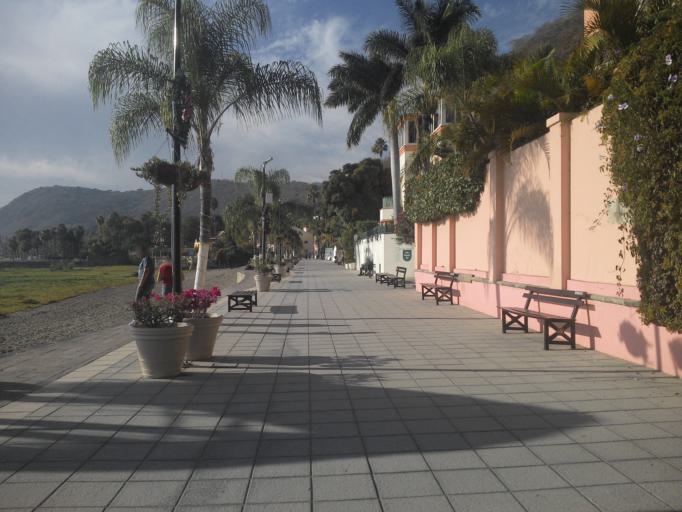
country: MX
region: Jalisco
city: Chapala
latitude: 20.2893
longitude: -103.1941
